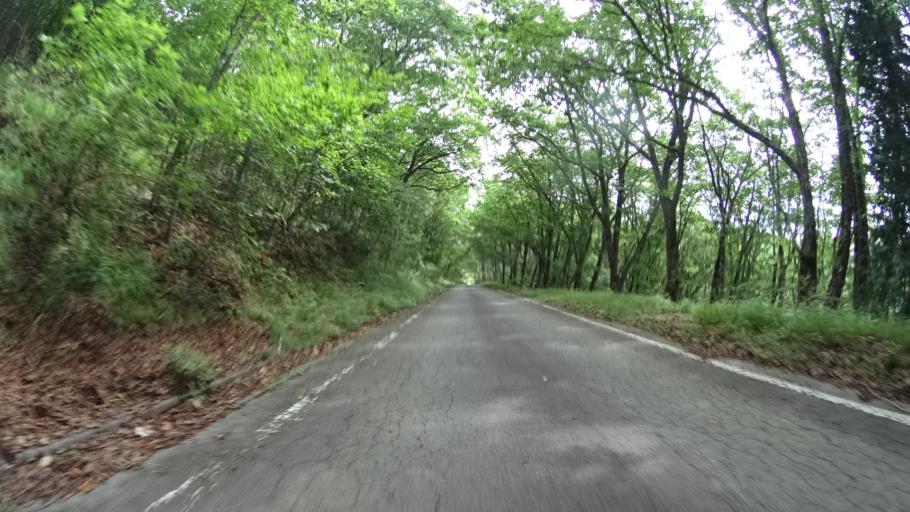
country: JP
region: Yamanashi
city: Kofu-shi
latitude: 35.8166
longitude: 138.5551
